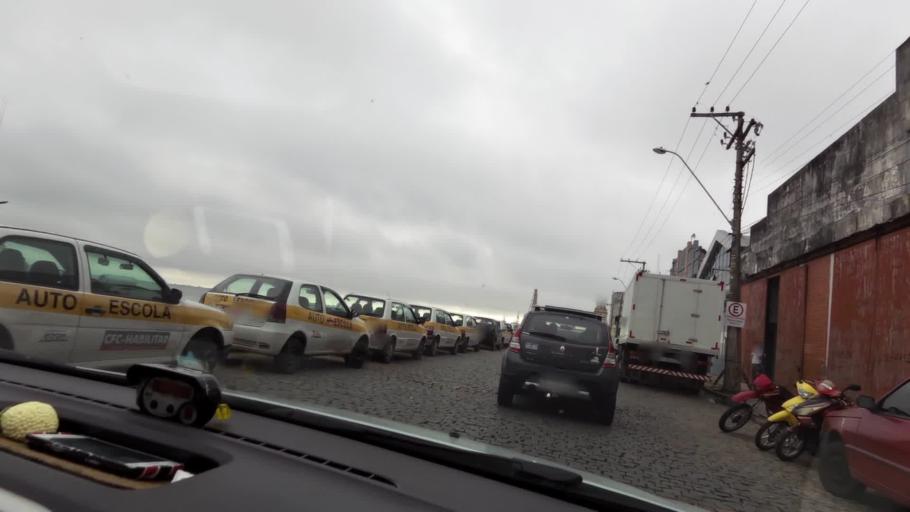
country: BR
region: Rio Grande do Sul
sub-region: Rio Grande
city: Rio Grande
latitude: -32.0344
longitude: -52.0921
